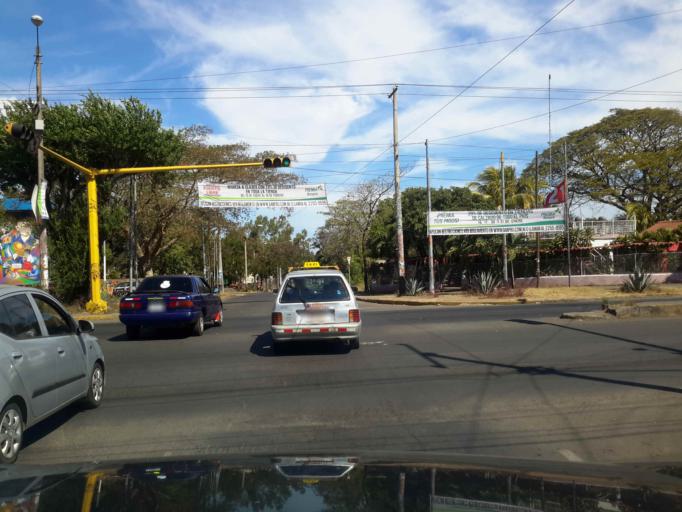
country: NI
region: Managua
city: Managua
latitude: 12.1256
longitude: -86.2956
